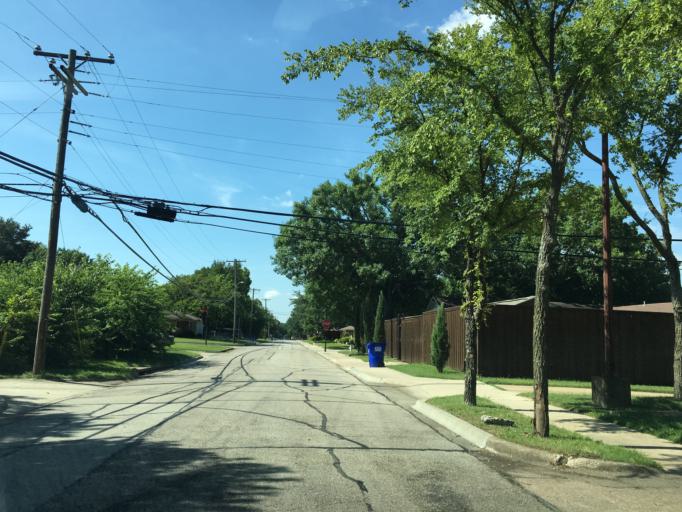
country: US
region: Texas
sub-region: Dallas County
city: Farmers Branch
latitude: 32.9224
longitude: -96.8792
